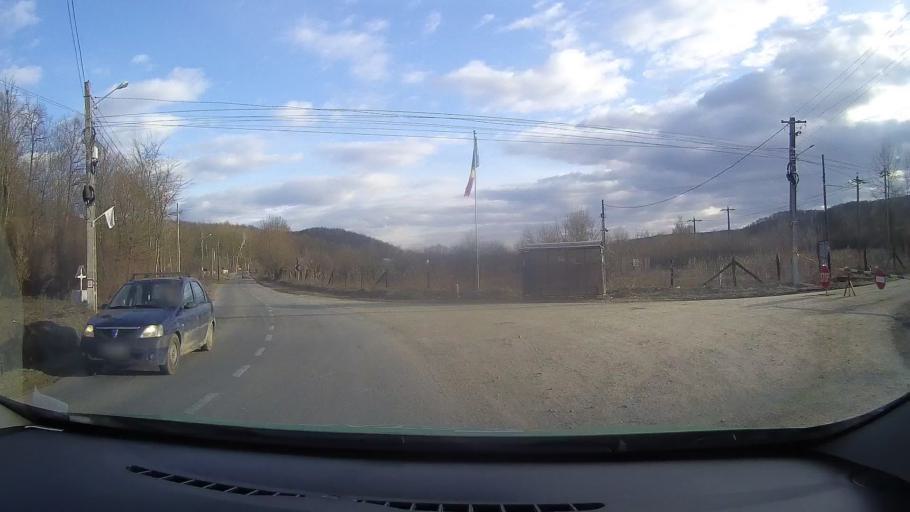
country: RO
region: Dambovita
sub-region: Comuna Ocnita
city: Ocnita
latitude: 44.9649
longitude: 25.5472
